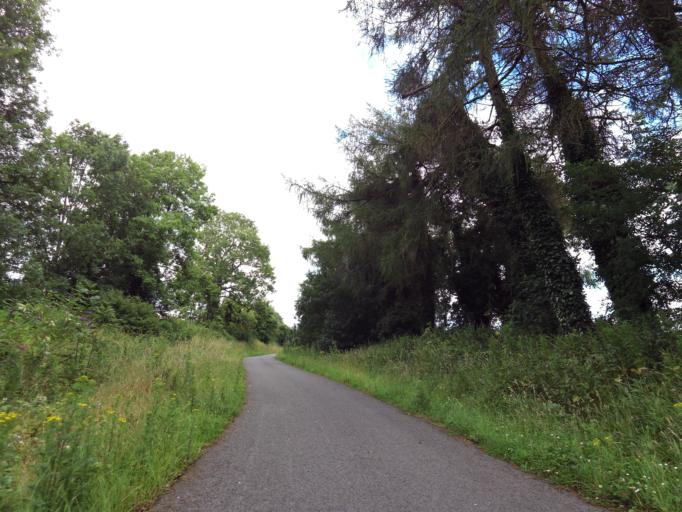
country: IE
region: Leinster
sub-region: An Iarmhi
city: Moate
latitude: 53.4005
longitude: -7.7053
